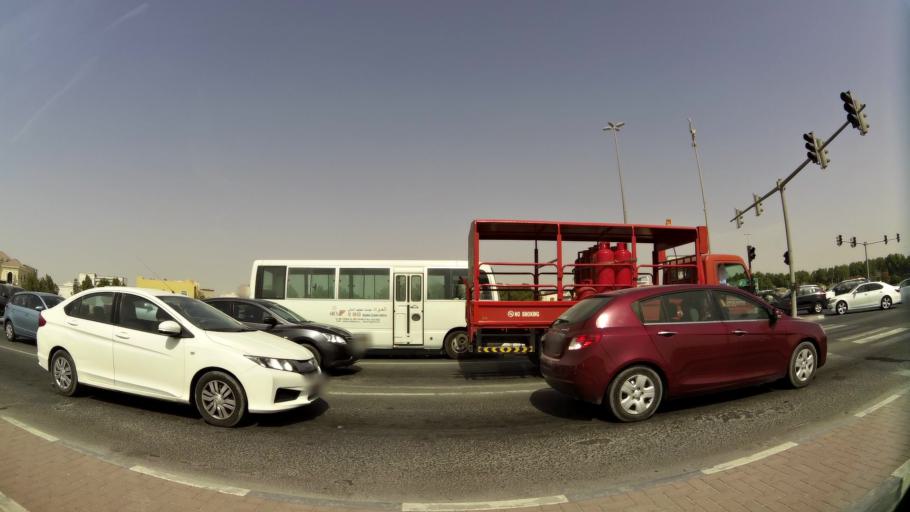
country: AE
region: Ash Shariqah
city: Sharjah
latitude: 25.2714
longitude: 55.3959
